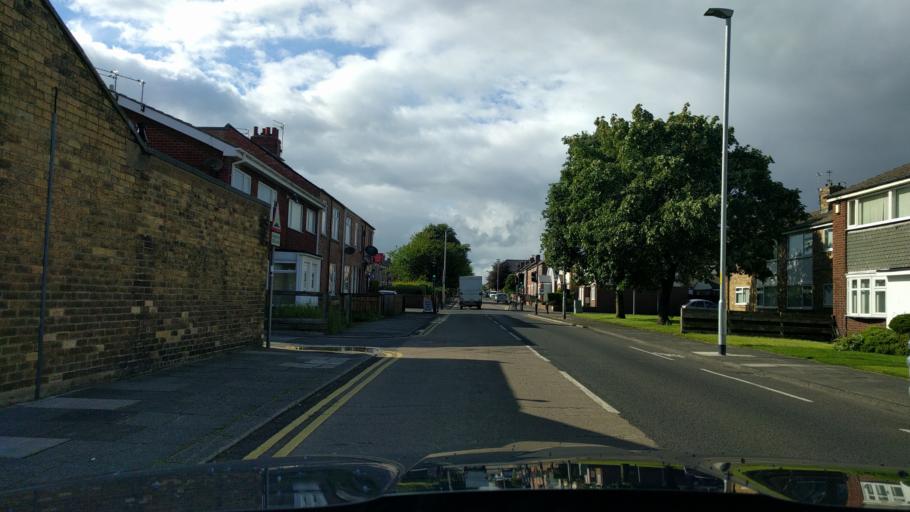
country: GB
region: England
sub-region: Northumberland
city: Ashington
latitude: 55.1753
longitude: -1.5579
